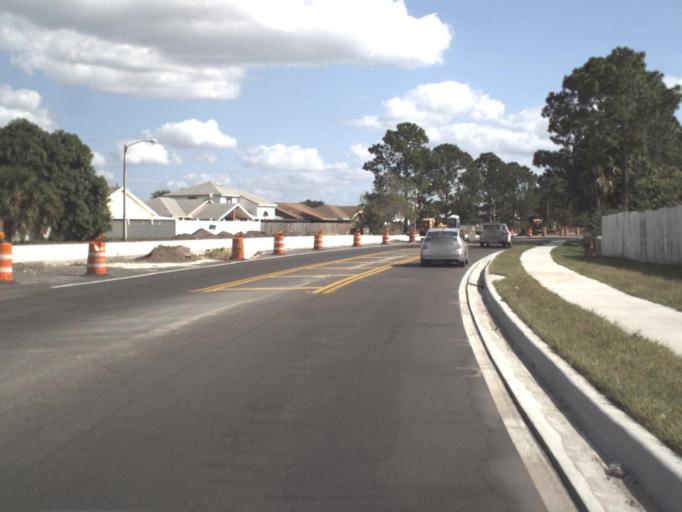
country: US
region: Florida
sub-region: Osceola County
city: Buenaventura Lakes
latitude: 28.3446
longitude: -81.3594
